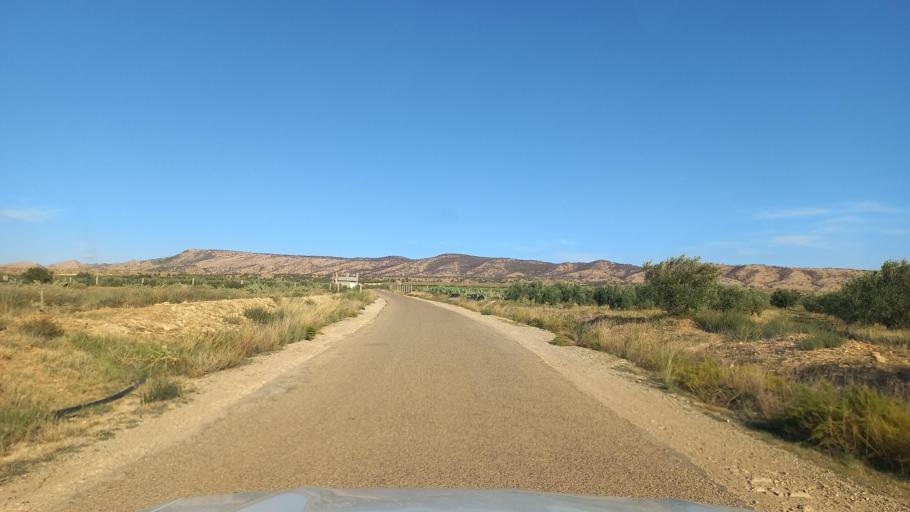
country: TN
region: Al Qasrayn
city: Sbiba
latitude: 35.3369
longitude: 9.1154
